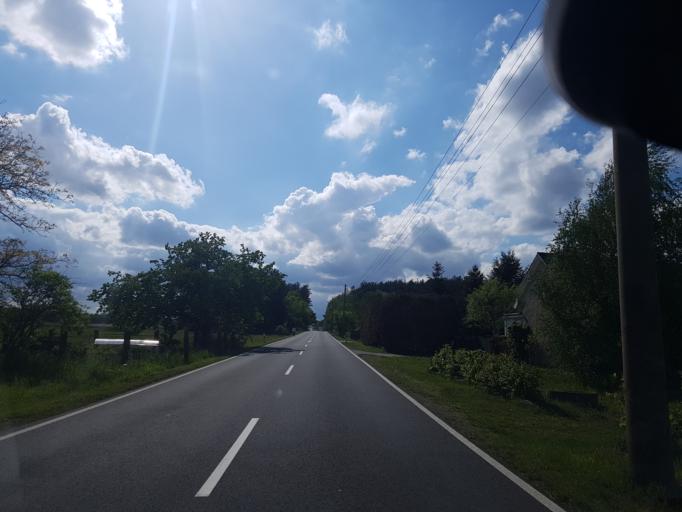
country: DE
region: Brandenburg
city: Drebkau
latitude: 51.6375
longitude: 14.2735
